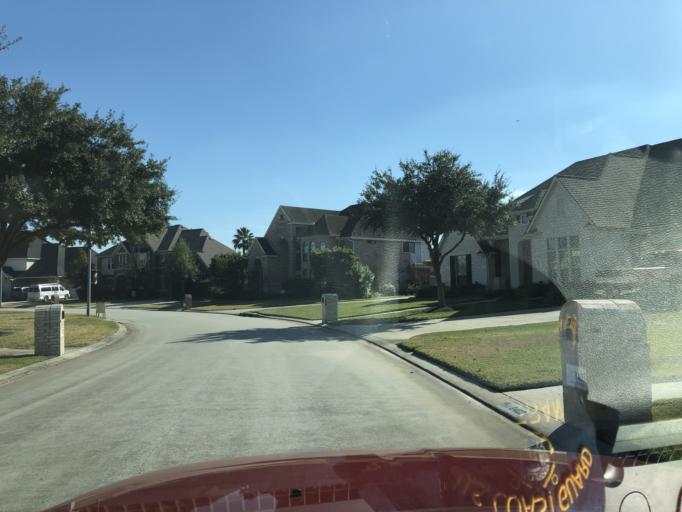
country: US
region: Texas
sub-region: Harris County
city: Tomball
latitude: 30.0363
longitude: -95.5482
